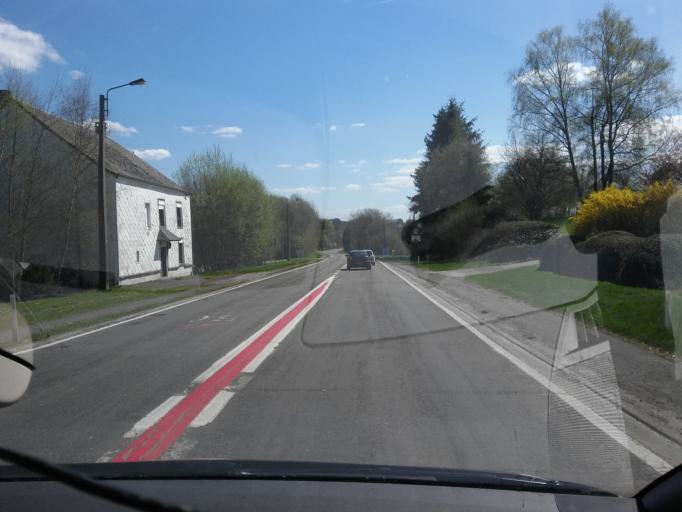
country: BE
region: Wallonia
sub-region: Province du Luxembourg
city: Neufchateau
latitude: 49.8938
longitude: 5.3871
